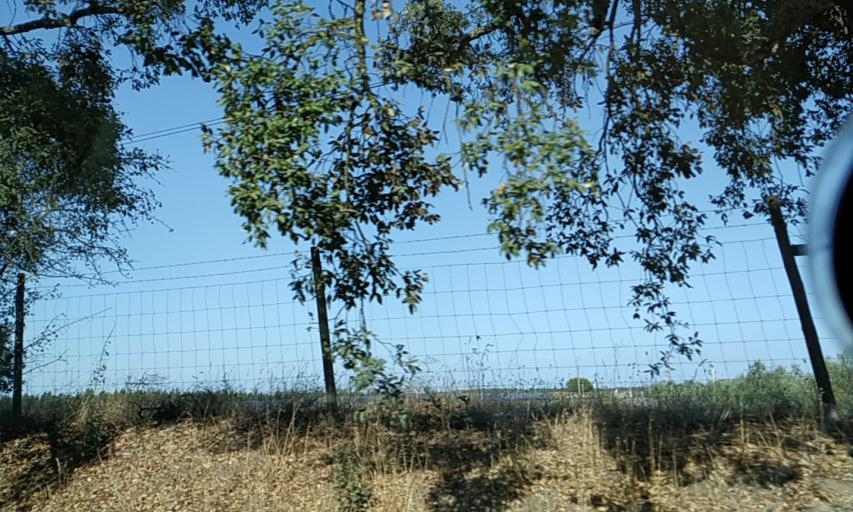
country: PT
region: Evora
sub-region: Vendas Novas
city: Vendas Novas
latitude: 38.7224
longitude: -8.6200
